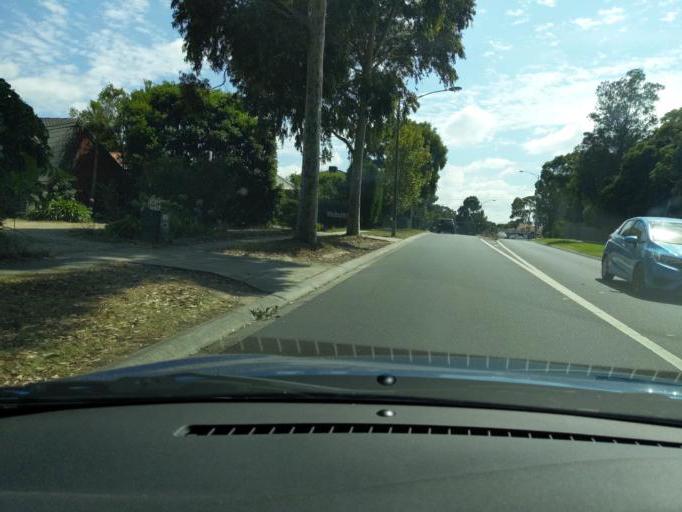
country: AU
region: Victoria
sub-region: Knox
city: Scoresby
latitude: -37.9133
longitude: 145.2467
